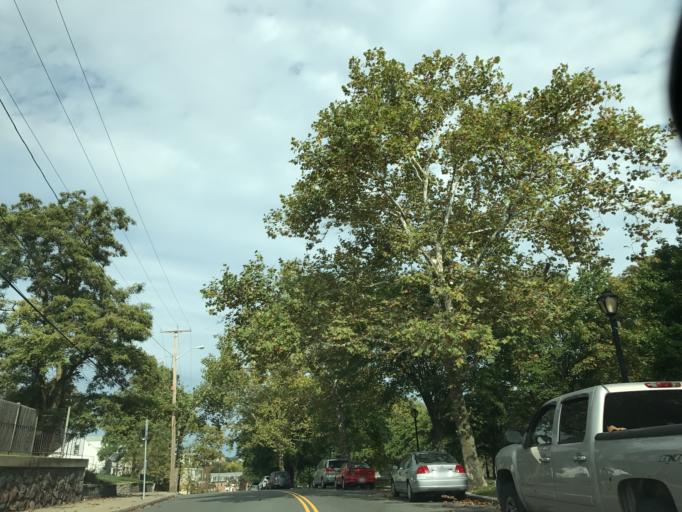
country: US
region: Massachusetts
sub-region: Middlesex County
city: Malden
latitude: 42.4238
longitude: -71.0562
